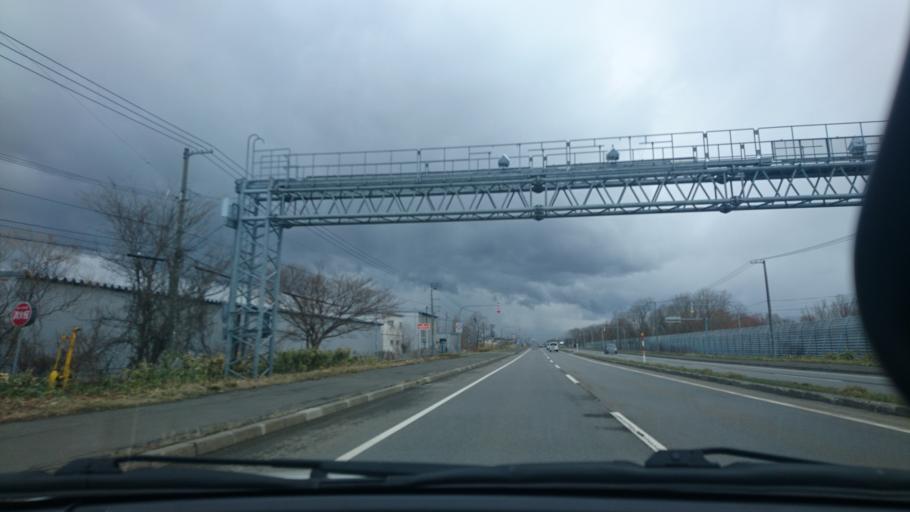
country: JP
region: Hokkaido
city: Ishikari
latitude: 43.2020
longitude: 141.3307
